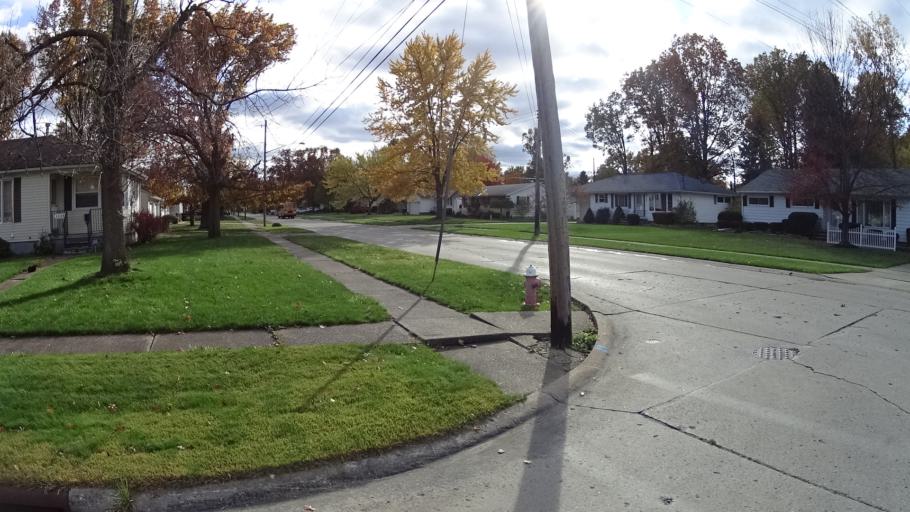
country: US
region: Ohio
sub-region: Lorain County
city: Lorain
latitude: 41.4237
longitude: -82.1898
